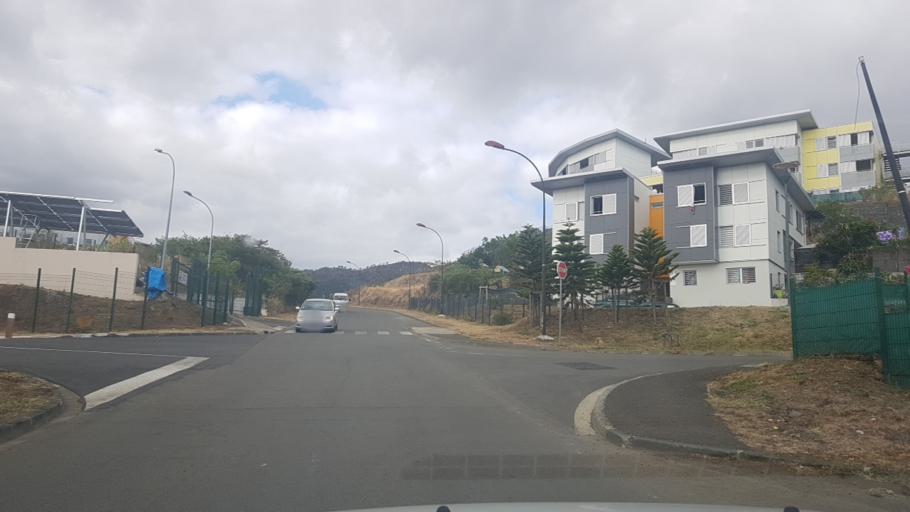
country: NC
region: South Province
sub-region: Dumbea
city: Dumbea
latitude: -22.2067
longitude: 166.4489
